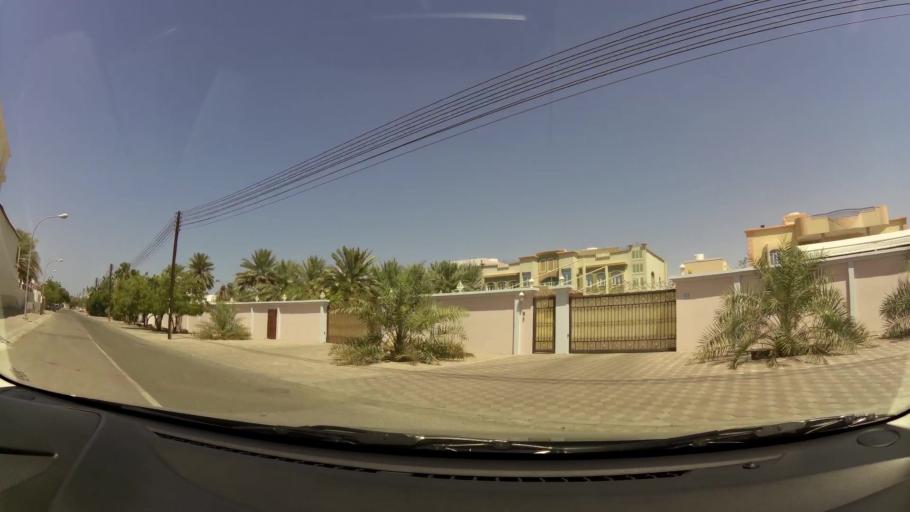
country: OM
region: Muhafazat Masqat
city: As Sib al Jadidah
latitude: 23.6265
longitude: 58.2275
